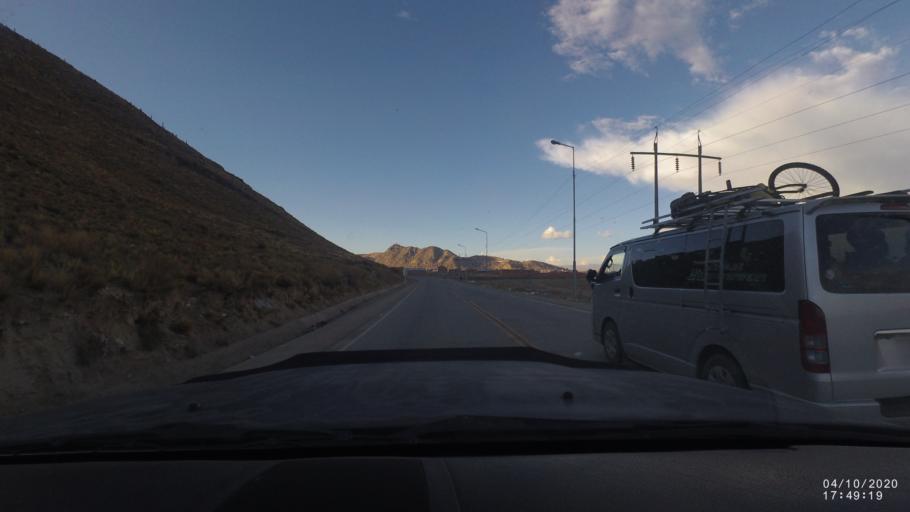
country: BO
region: Oruro
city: Oruro
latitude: -18.0125
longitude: -67.1372
